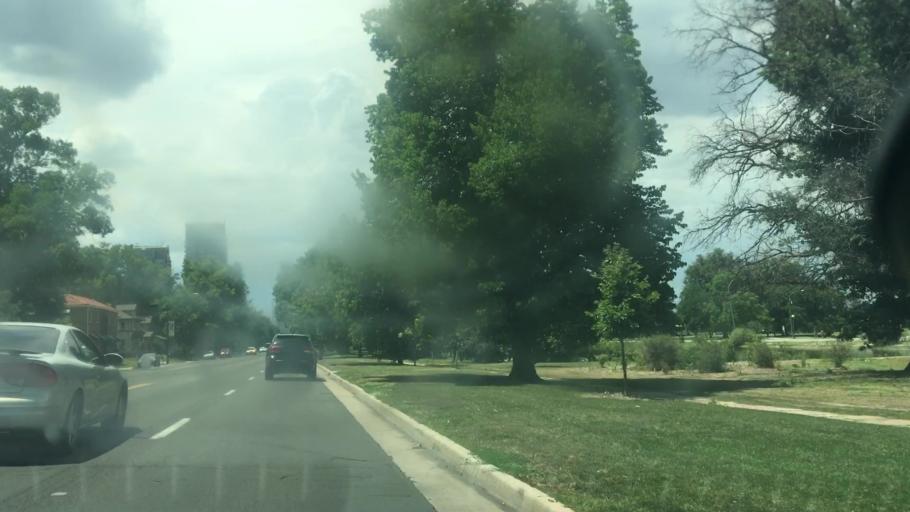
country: US
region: Colorado
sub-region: Denver County
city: Denver
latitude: 39.7438
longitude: -104.9450
